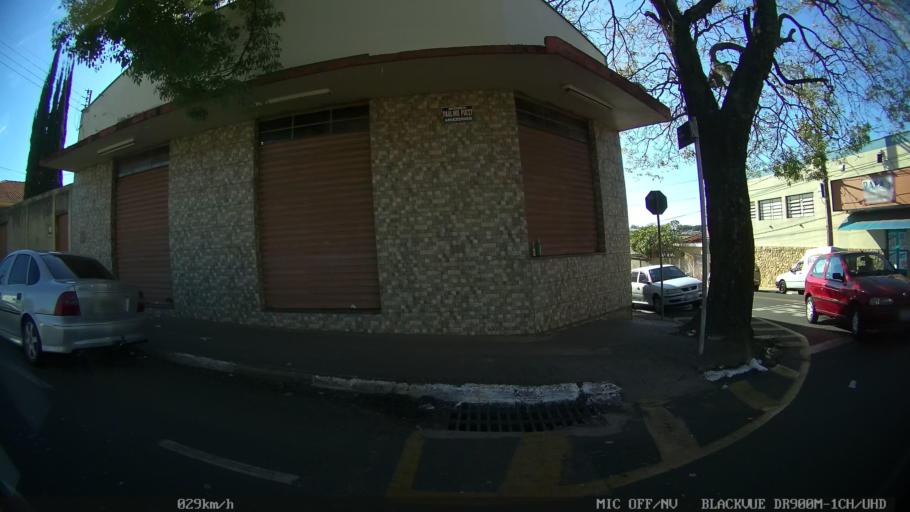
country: BR
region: Sao Paulo
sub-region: Franca
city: Franca
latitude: -20.5434
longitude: -47.4116
